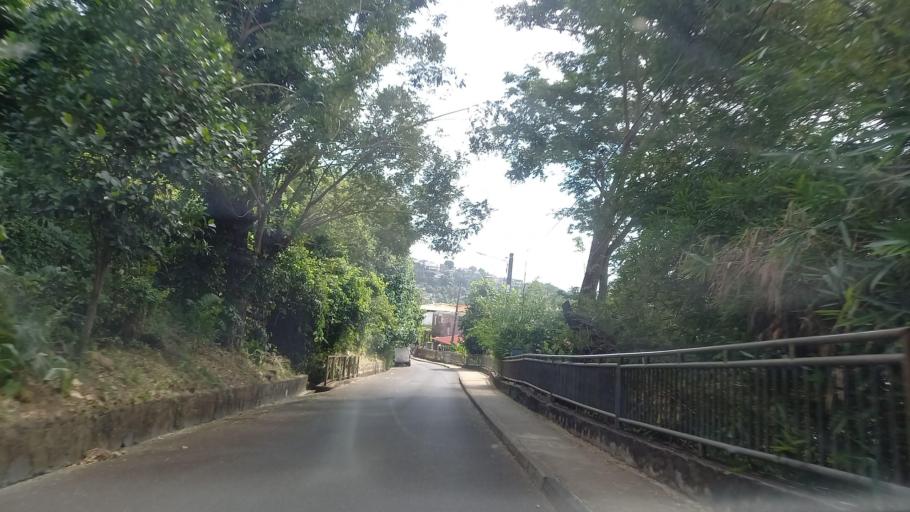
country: YT
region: Sada
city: Sada
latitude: -12.8460
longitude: 45.1019
